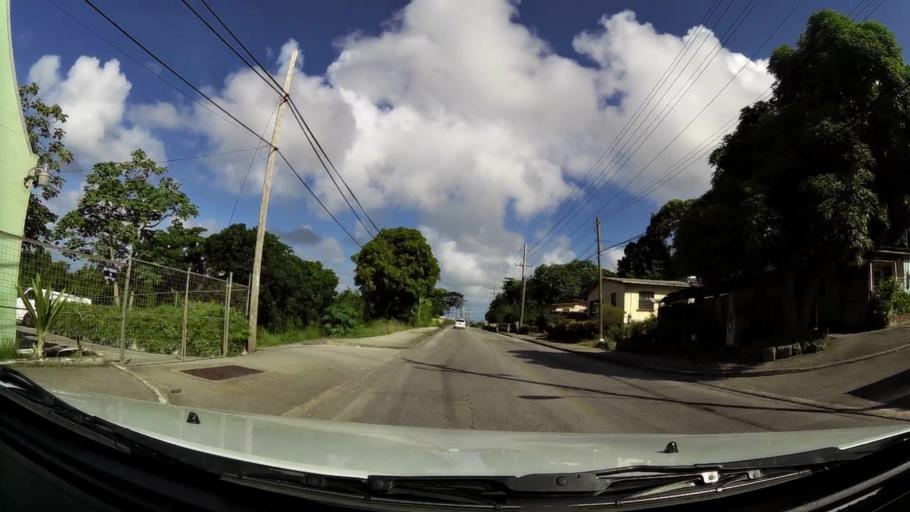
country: BB
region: Saint Peter
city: Speightstown
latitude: 13.2261
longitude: -59.6224
